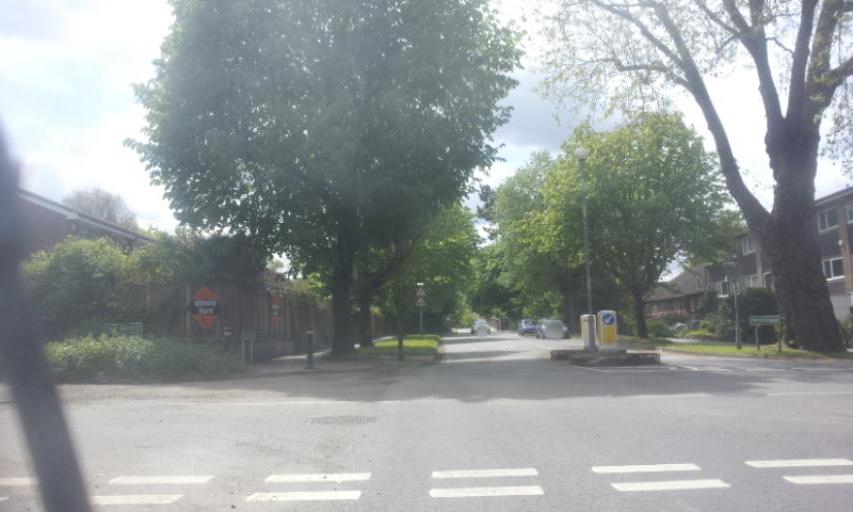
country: GB
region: England
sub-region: Greater London
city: Beckenham
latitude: 51.4111
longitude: -0.0153
